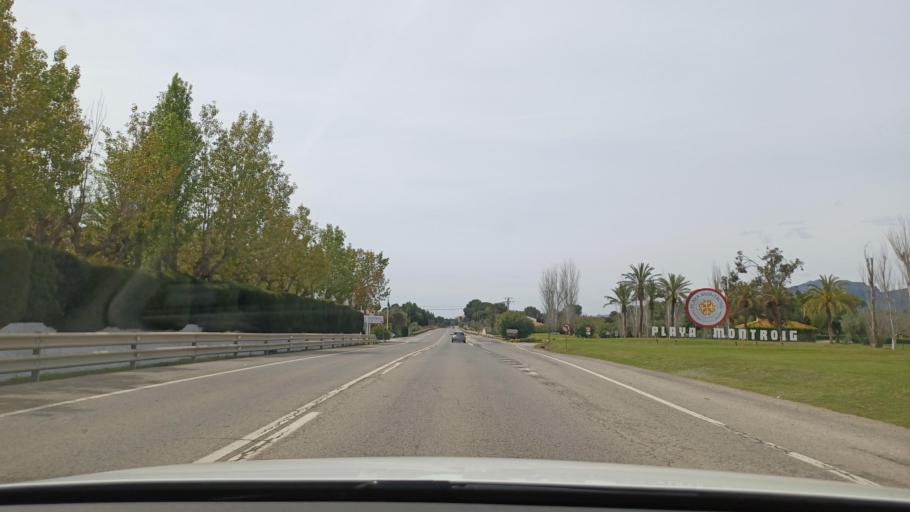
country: ES
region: Catalonia
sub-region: Provincia de Tarragona
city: Vilanova d'Escornalbou
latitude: 41.0353
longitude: 0.9696
